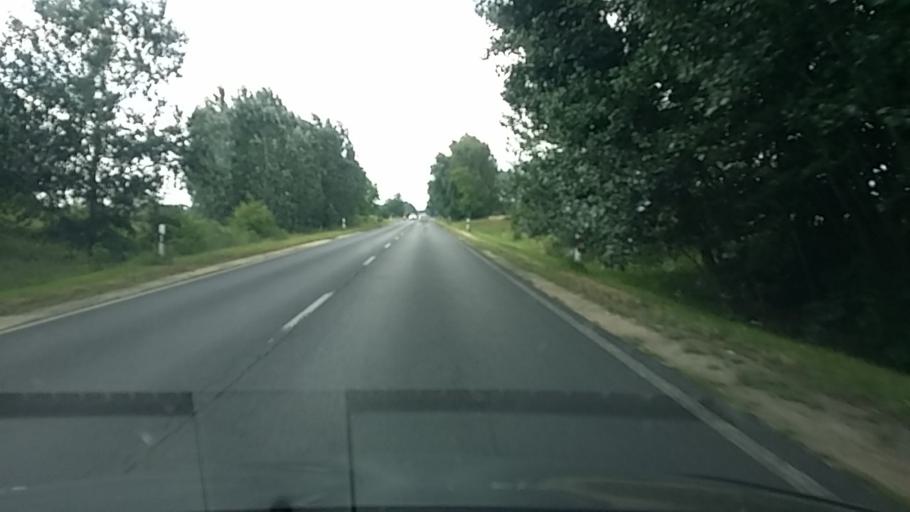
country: HU
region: Pest
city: Taborfalva
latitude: 47.1091
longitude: 19.4582
